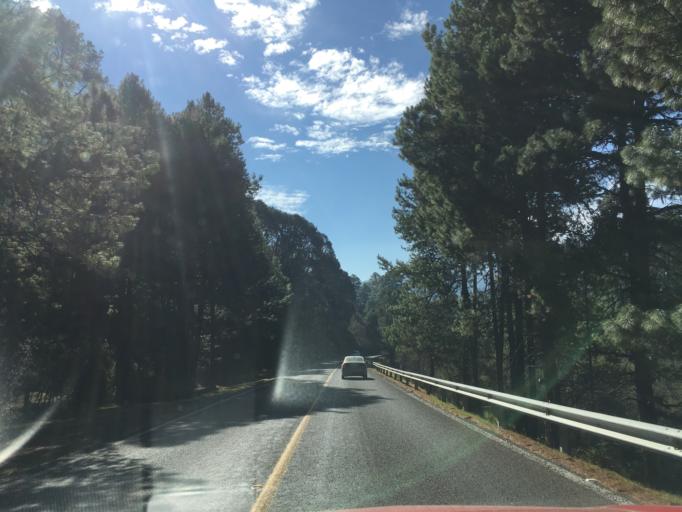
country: MX
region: Michoacan
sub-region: Hidalgo
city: Tierras Coloradas (San Pedro)
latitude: 19.6909
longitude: -100.7431
